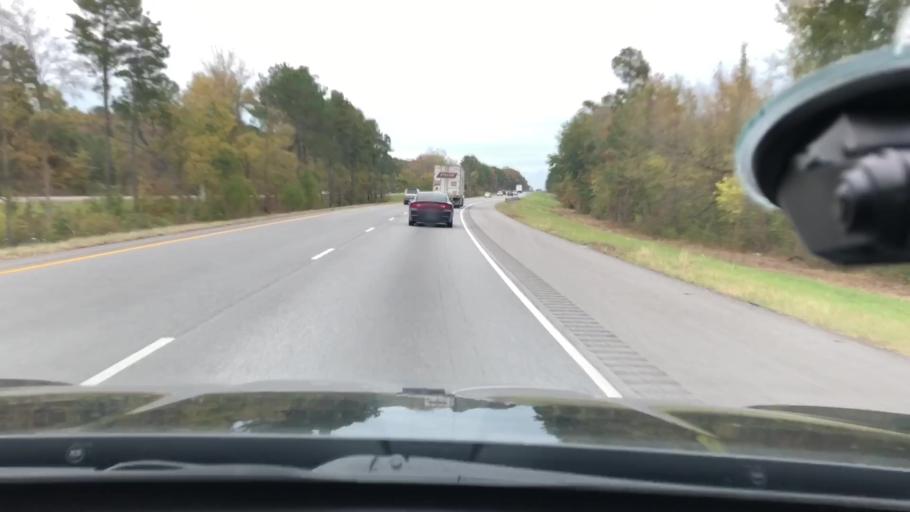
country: US
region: Arkansas
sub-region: Hempstead County
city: Hope
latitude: 33.6205
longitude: -93.7862
